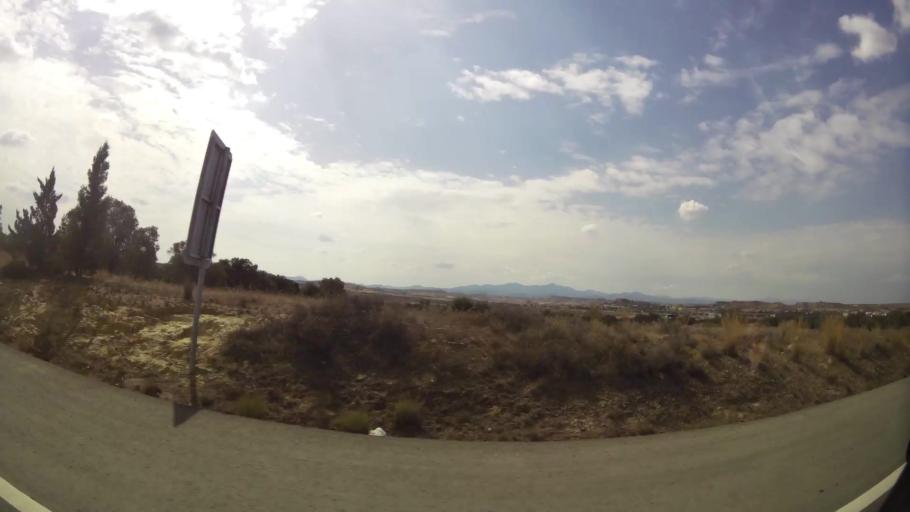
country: CY
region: Lefkosia
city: Tseri
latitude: 35.0651
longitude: 33.3391
